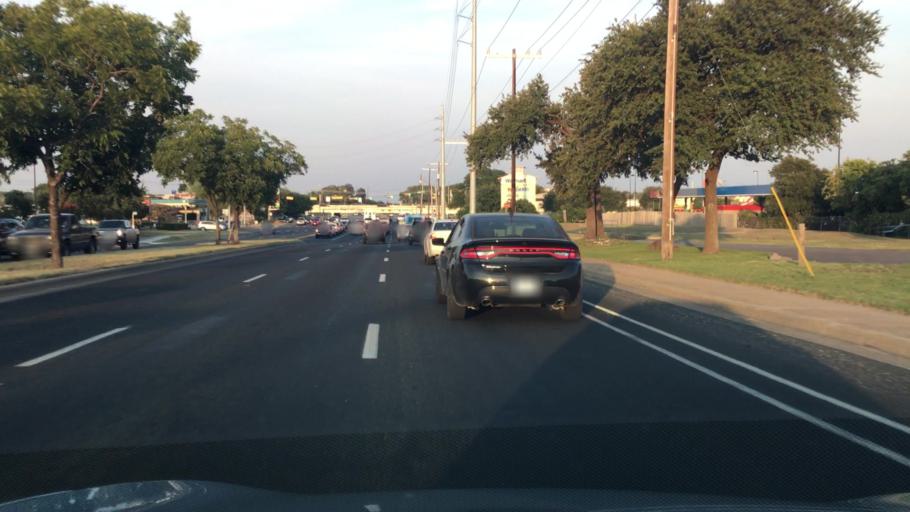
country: US
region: Texas
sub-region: Travis County
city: Onion Creek
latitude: 30.1671
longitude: -97.7902
